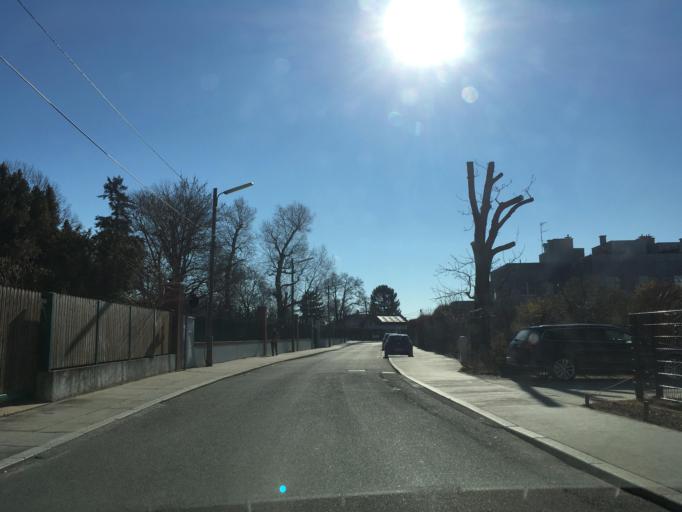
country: AT
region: Lower Austria
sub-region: Politischer Bezirk Ganserndorf
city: Gross-Enzersdorf
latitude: 48.2149
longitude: 16.4885
